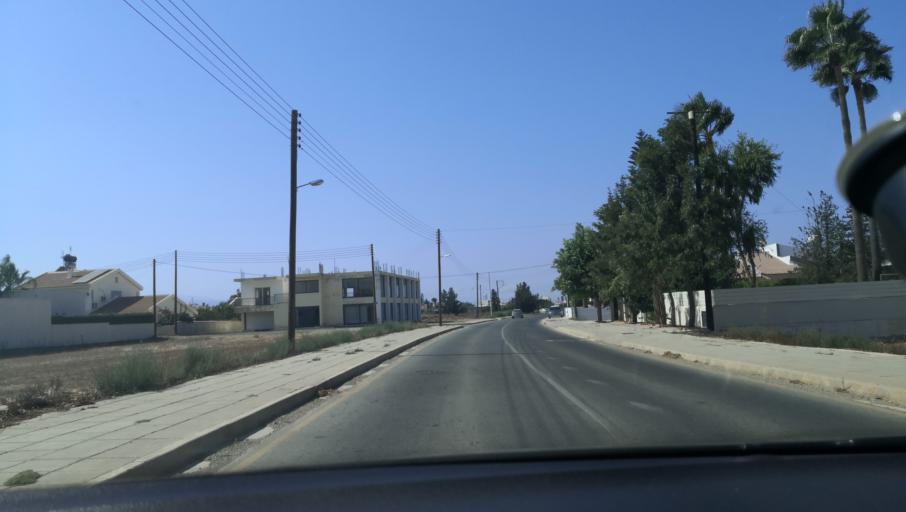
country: CY
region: Lefkosia
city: Kokkinotrimithia
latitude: 35.1149
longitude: 33.2189
